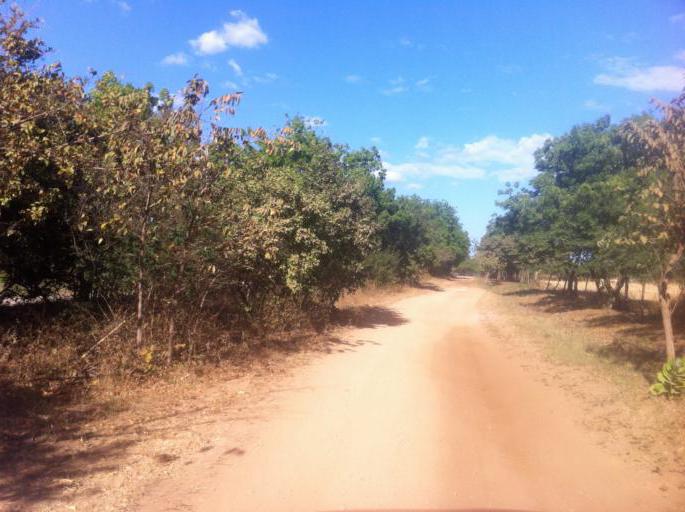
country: NI
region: Managua
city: Carlos Fonseca Amador
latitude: 11.9112
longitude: -86.6090
